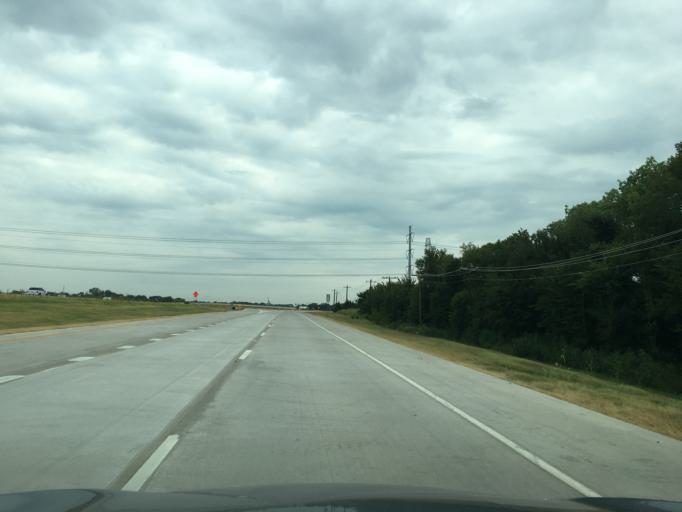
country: US
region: Texas
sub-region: Collin County
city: Melissa
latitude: 33.3141
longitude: -96.5902
